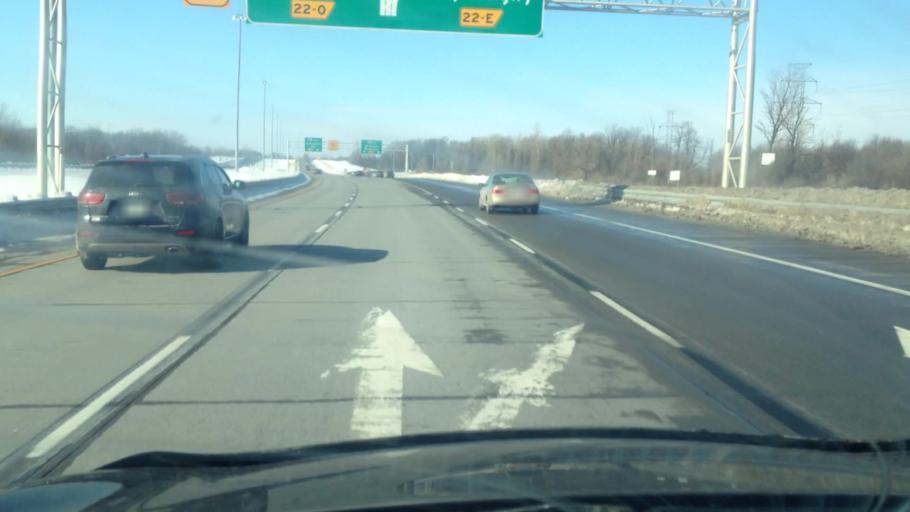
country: CA
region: Quebec
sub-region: Laurentides
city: Boisbriand
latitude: 45.5949
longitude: -73.8533
